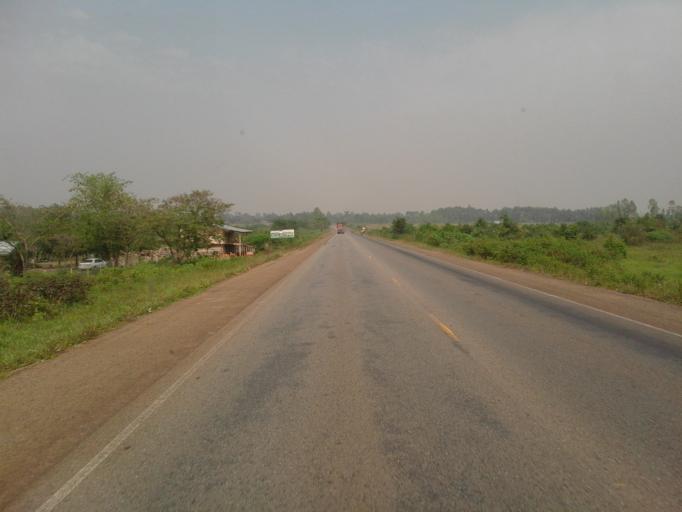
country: UG
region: Eastern Region
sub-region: Bugiri District
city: Bugiri
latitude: 0.5916
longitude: 33.7205
